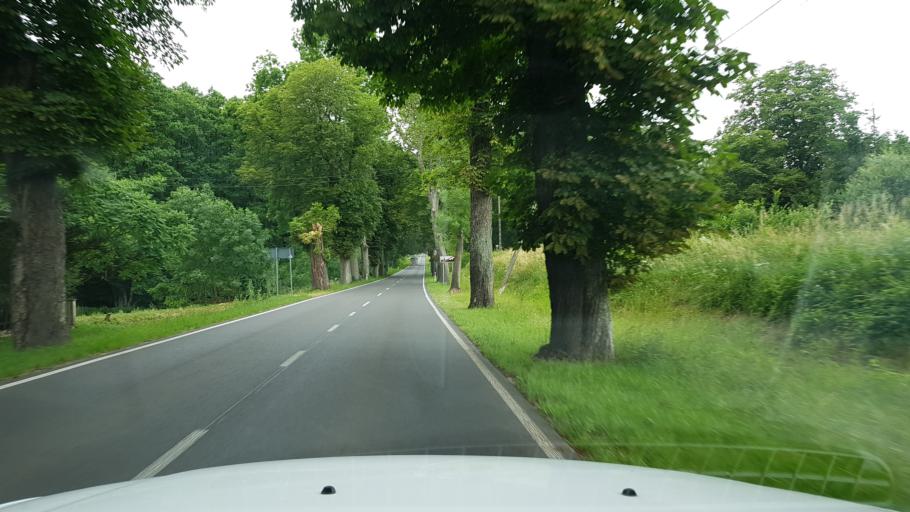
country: PL
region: West Pomeranian Voivodeship
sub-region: Powiat gryficki
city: Gryfice
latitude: 53.9050
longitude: 15.1486
